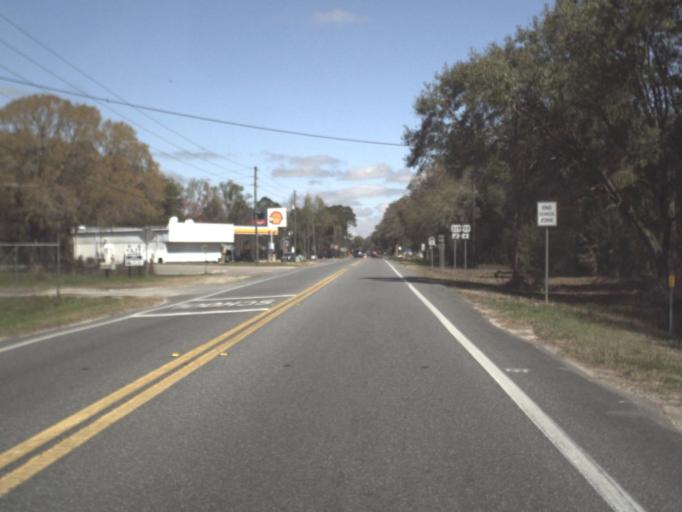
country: US
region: Florida
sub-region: Wakulla County
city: Crawfordville
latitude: 30.0816
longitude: -84.3883
